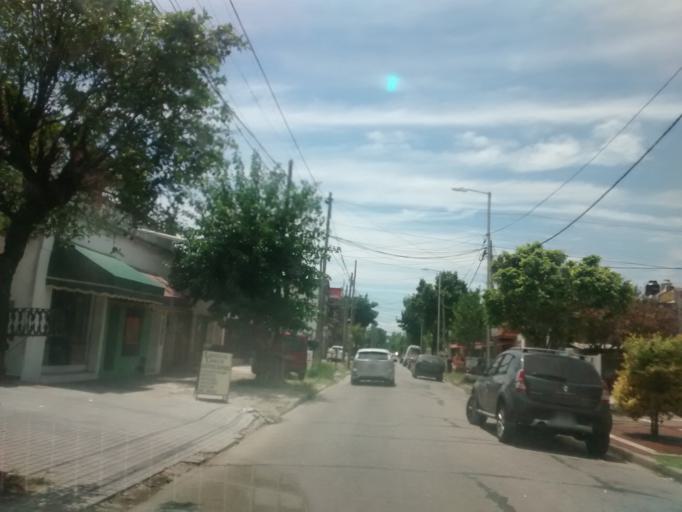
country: AR
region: Buenos Aires
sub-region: Partido de Avellaneda
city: Avellaneda
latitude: -34.6925
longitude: -58.3233
